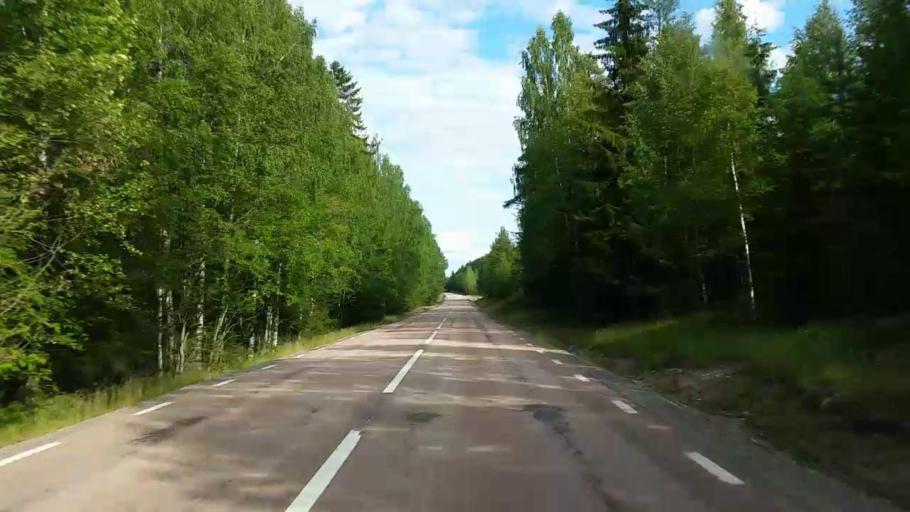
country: SE
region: Gaevleborg
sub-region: Ljusdals Kommun
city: Farila
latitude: 61.8811
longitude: 15.9430
